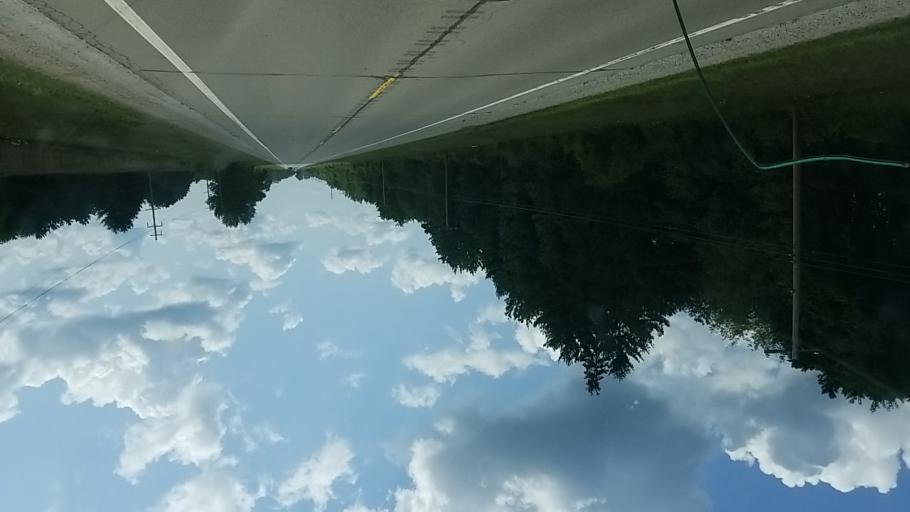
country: US
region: Michigan
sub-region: Muskegon County
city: Ravenna
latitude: 43.2350
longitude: -85.9995
